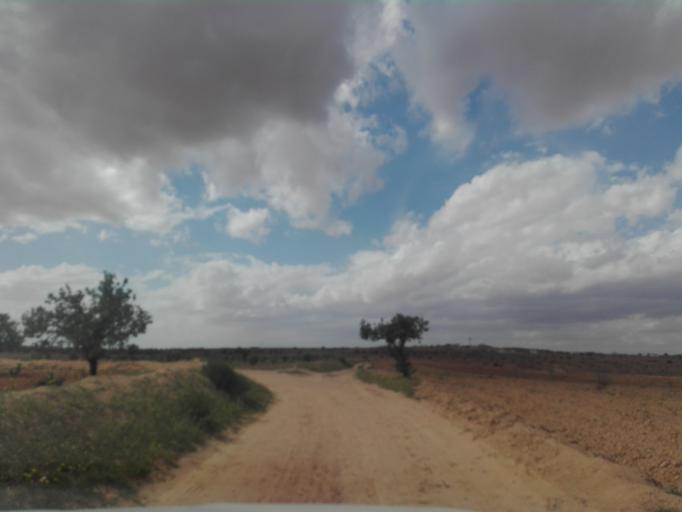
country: TN
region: Safaqis
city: Sfax
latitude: 34.6970
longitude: 10.4444
